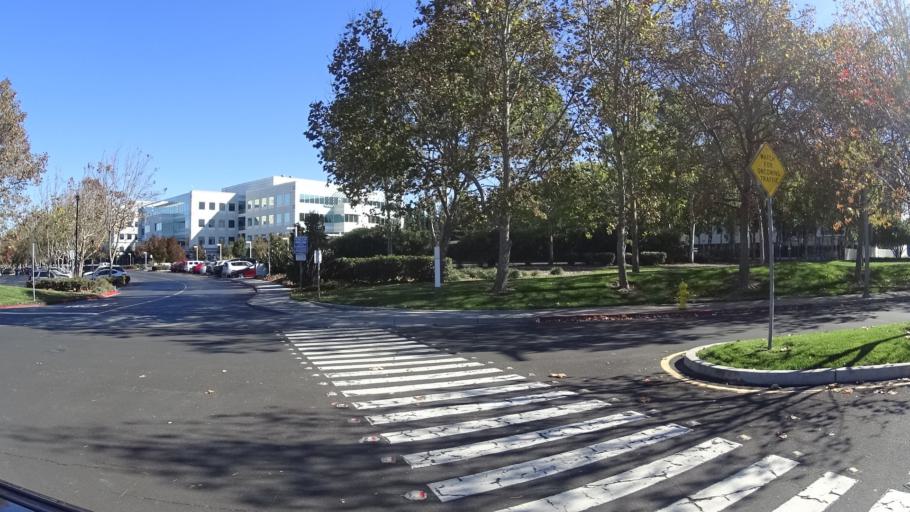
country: US
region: California
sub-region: Santa Clara County
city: Santa Clara
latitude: 37.3766
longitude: -121.9247
